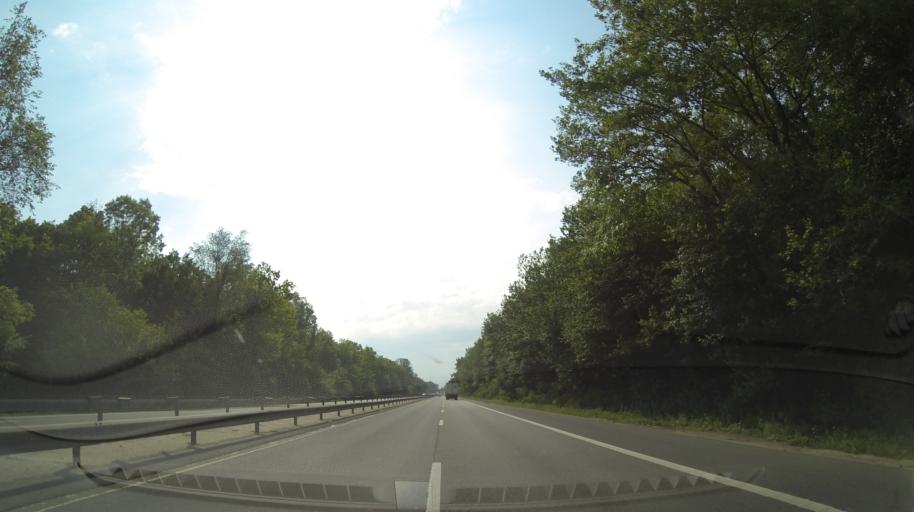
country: RO
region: Giurgiu
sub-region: Comuna Vanatorii Mici
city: Vanatorii Mici
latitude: 44.5076
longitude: 25.5722
